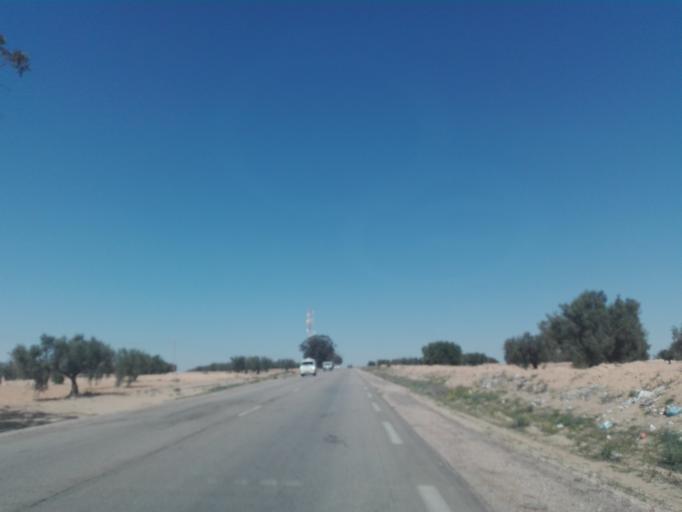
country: TN
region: Safaqis
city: Bi'r `Ali Bin Khalifah
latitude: 34.7548
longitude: 10.3335
